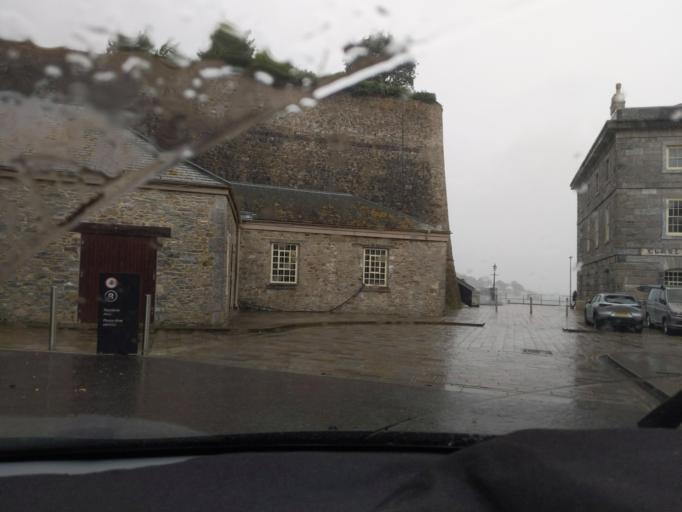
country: GB
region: England
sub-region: Cornwall
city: Millbrook
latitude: 50.3604
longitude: -4.1663
